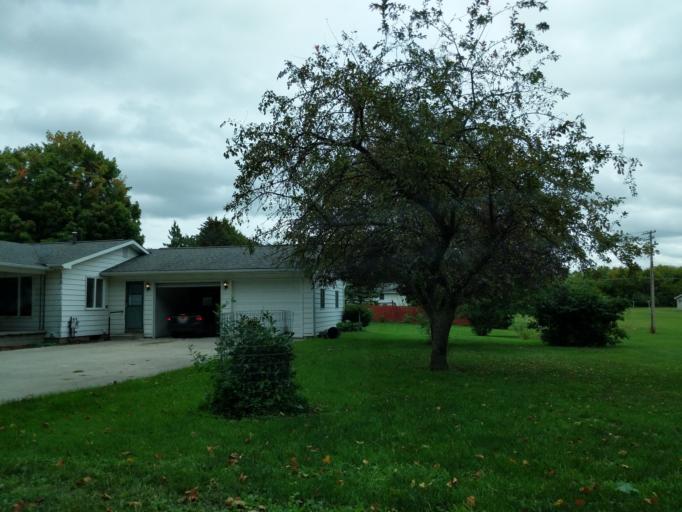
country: US
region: Michigan
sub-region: Lapeer County
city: Barnes Lake-Millers Lake
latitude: 43.3313
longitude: -83.3488
